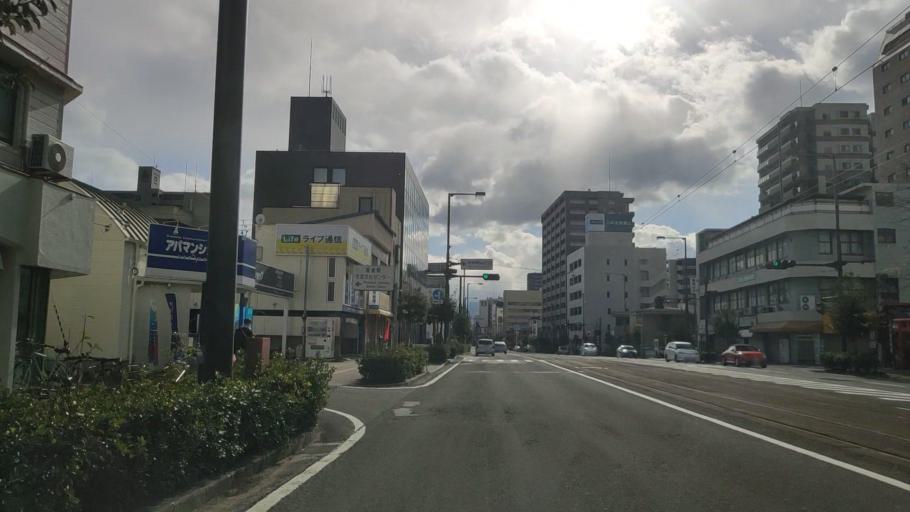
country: JP
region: Ehime
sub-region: Shikoku-chuo Shi
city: Matsuyama
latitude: 33.8458
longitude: 132.7755
